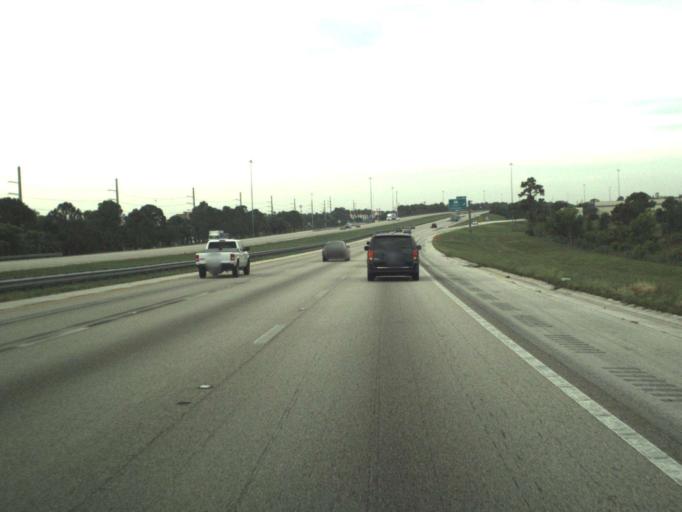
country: US
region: Florida
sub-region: Martin County
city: Palm City
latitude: 27.1160
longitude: -80.2660
